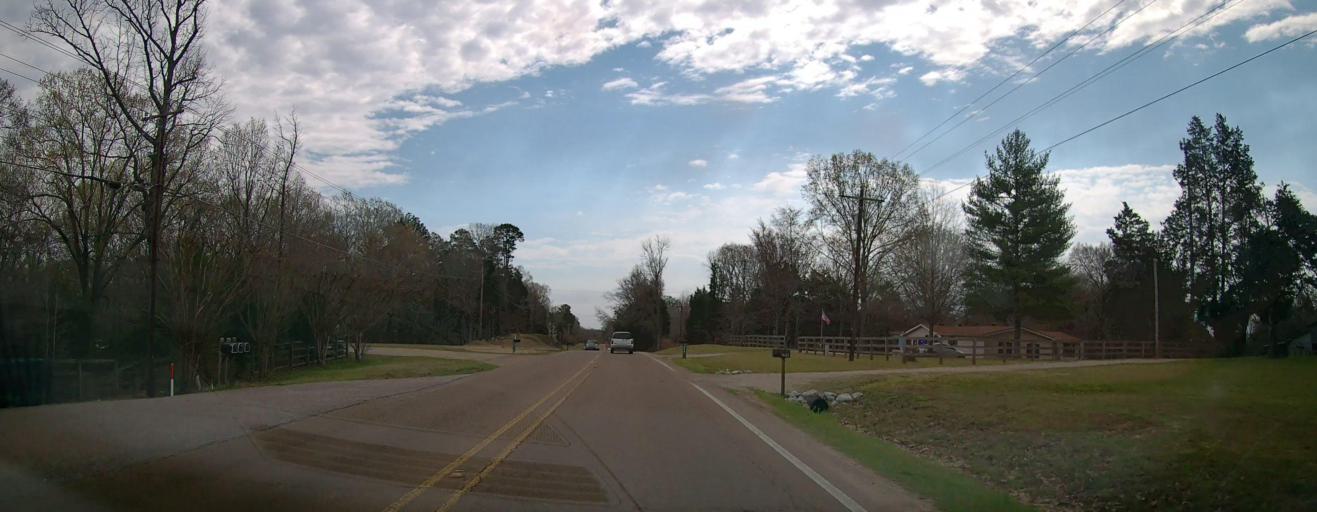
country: US
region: Mississippi
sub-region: De Soto County
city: Olive Branch
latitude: 34.9243
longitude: -89.7818
